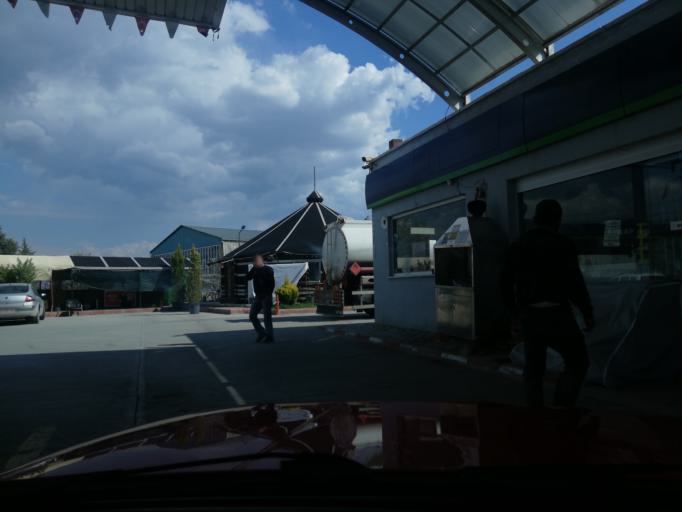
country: TR
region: Burdur
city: Celtikci
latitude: 37.5218
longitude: 30.5147
